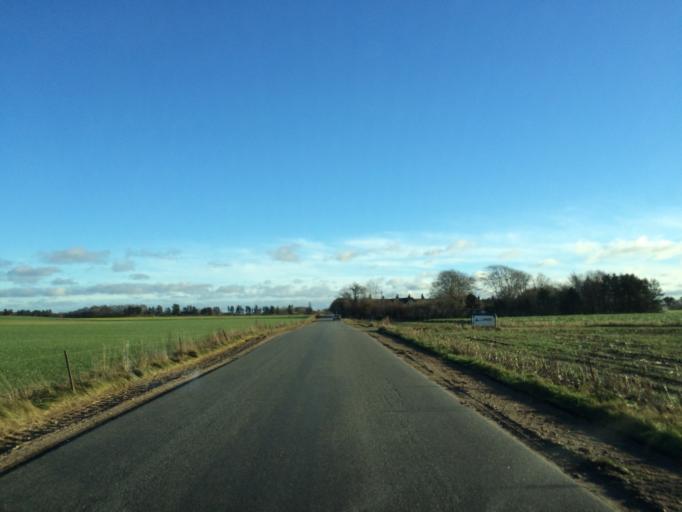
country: DK
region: Central Jutland
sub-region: Herning Kommune
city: Kibaek
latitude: 56.0489
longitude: 8.7998
